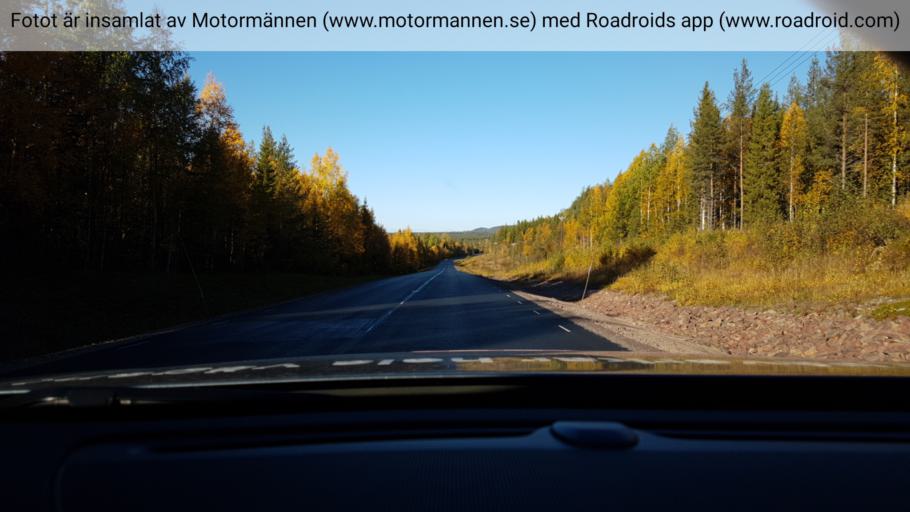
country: SE
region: Vaesterbotten
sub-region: Skelleftea Kommun
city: Langsele
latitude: 65.4033
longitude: 19.9362
